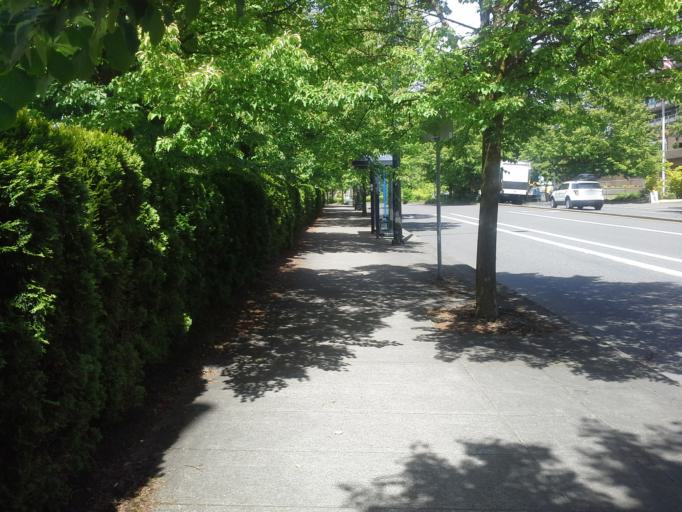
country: US
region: Oregon
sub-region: Multnomah County
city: Portland
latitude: 45.5317
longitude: -122.6496
